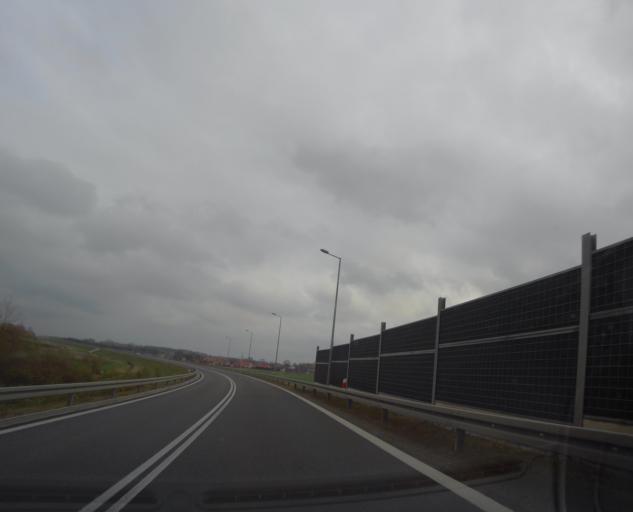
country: PL
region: Subcarpathian Voivodeship
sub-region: Powiat lezajski
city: Giedlarowa
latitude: 50.2398
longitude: 22.4167
